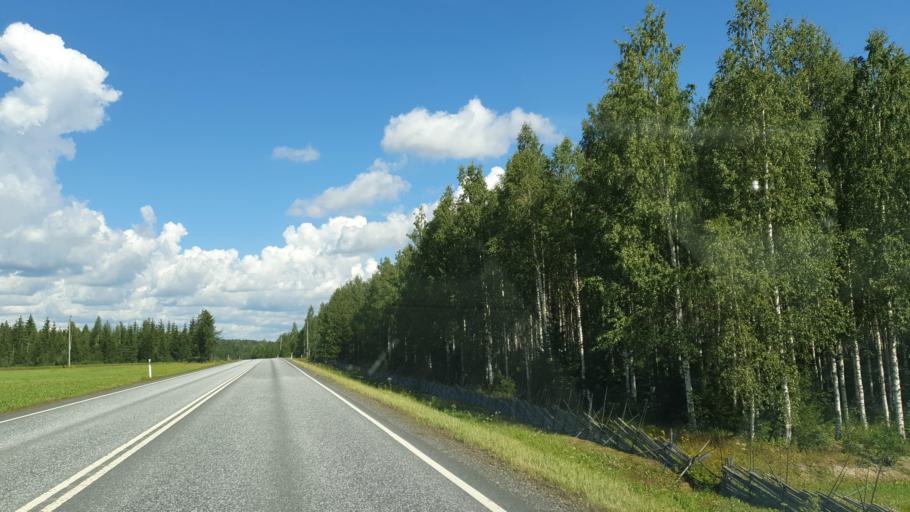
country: FI
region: Northern Savo
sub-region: Ylae-Savo
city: Sonkajaervi
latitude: 63.8091
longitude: 27.4191
